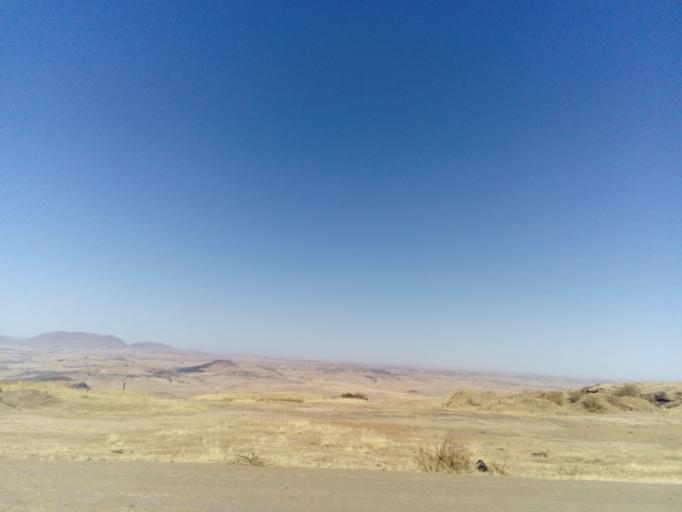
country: LS
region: Berea
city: Teyateyaneng
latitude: -29.1274
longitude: 27.8347
